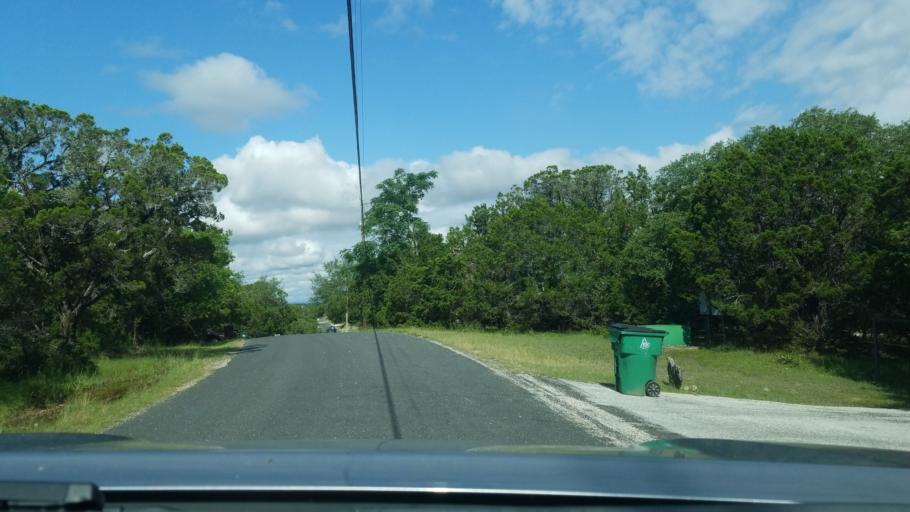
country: US
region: Texas
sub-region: Comal County
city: Bulverde
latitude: 29.7658
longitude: -98.4446
